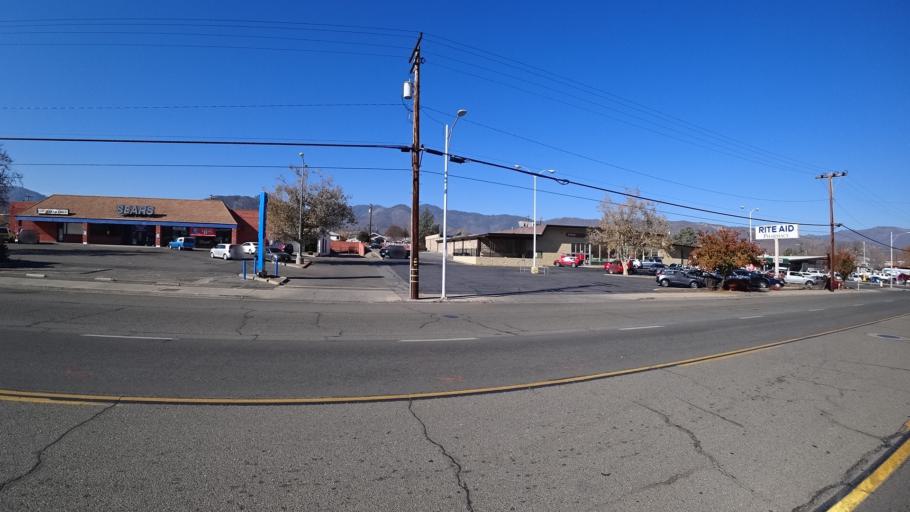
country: US
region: California
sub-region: Siskiyou County
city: Yreka
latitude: 41.7252
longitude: -122.6385
